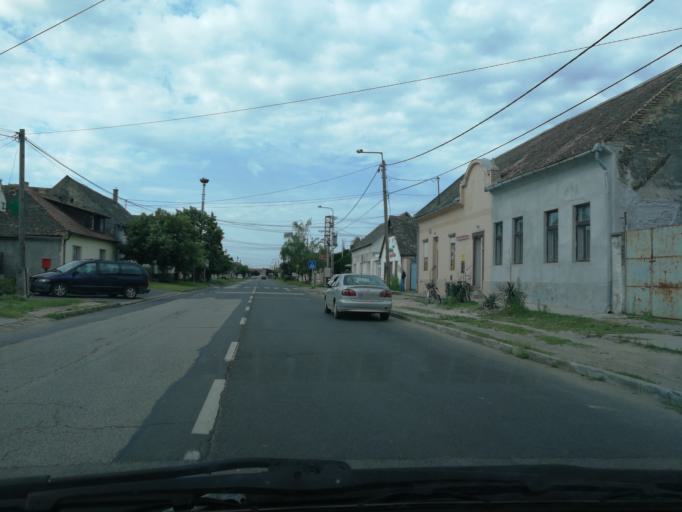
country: HU
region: Bacs-Kiskun
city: Baja
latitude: 46.2056
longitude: 18.9604
